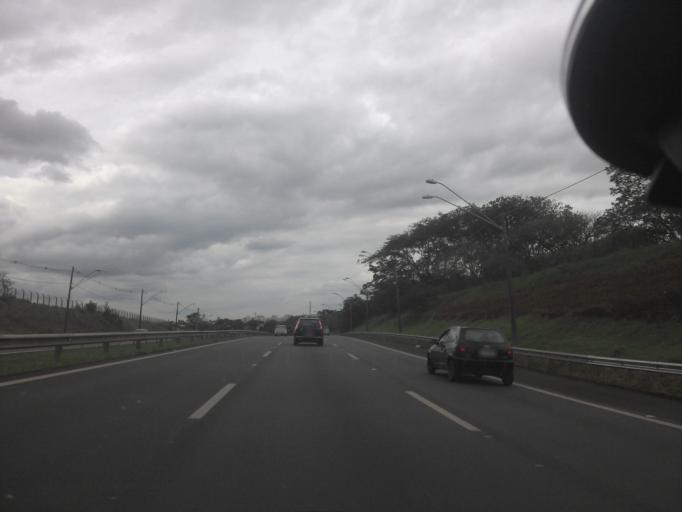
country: BR
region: Sao Paulo
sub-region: Campinas
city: Campinas
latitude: -22.8660
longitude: -47.0711
